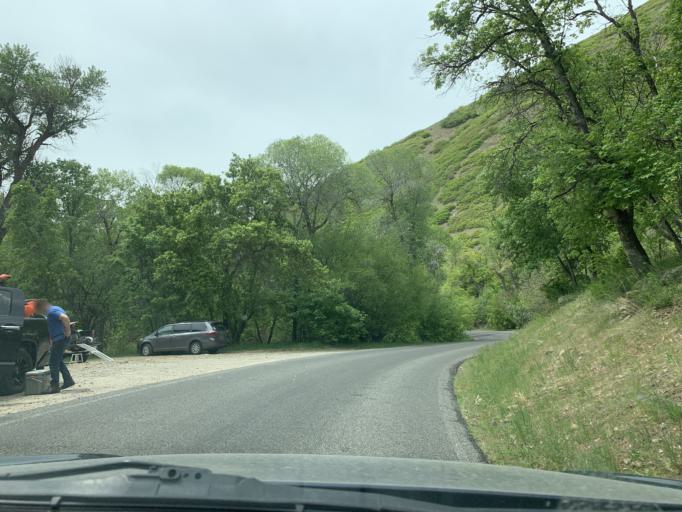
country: US
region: Utah
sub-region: Utah County
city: Mapleton
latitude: 40.1705
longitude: -111.4742
